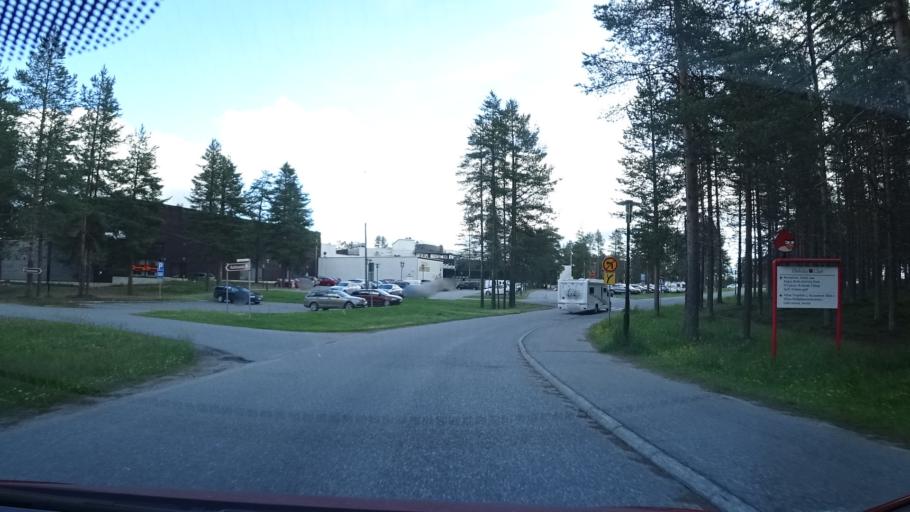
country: FI
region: Northern Ostrobothnia
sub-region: Koillismaa
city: Kuusamo
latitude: 66.0007
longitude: 29.1636
